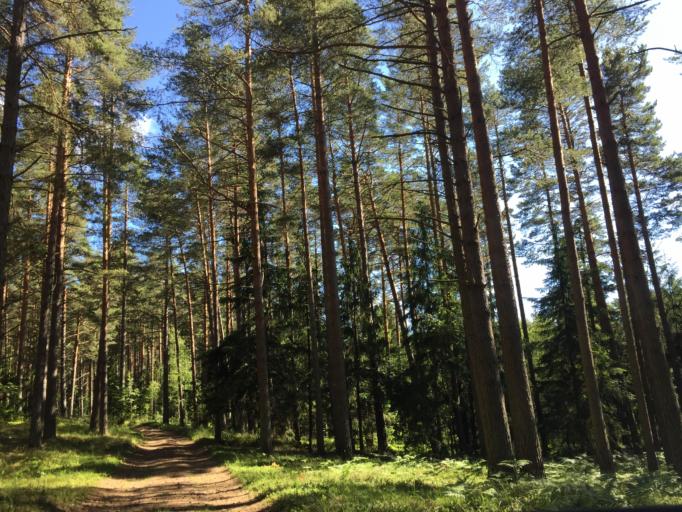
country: LV
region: Ventspils
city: Ventspils
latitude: 57.4677
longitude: 21.6511
